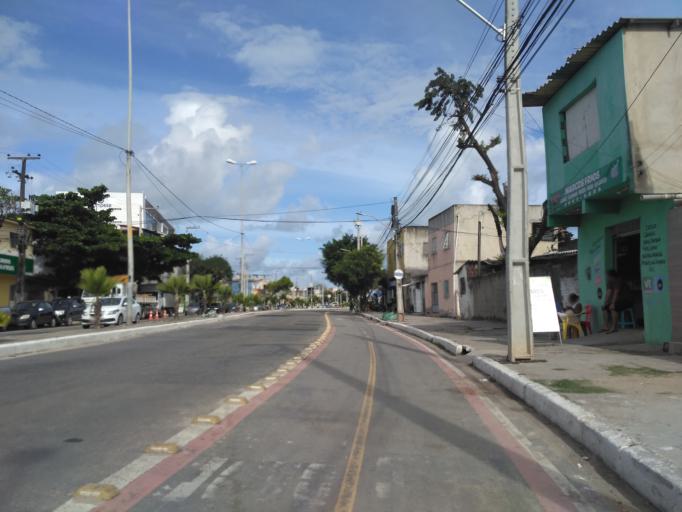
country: BR
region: Pernambuco
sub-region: Recife
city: Recife
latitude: -8.0408
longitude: -34.8784
